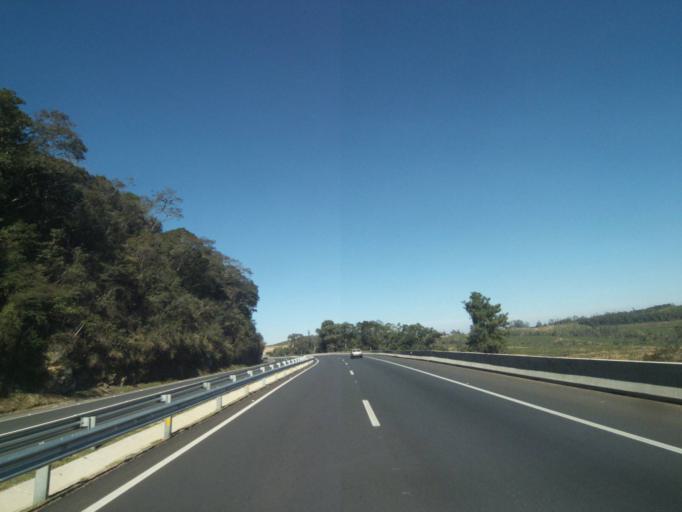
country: BR
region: Parana
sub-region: Tibagi
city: Tibagi
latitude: -24.8101
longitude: -50.4906
